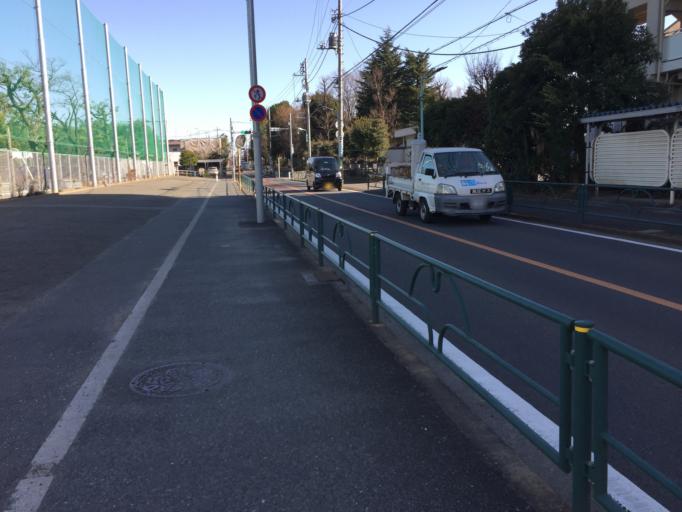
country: JP
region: Tokyo
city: Chofugaoka
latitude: 35.6253
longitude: 139.5943
